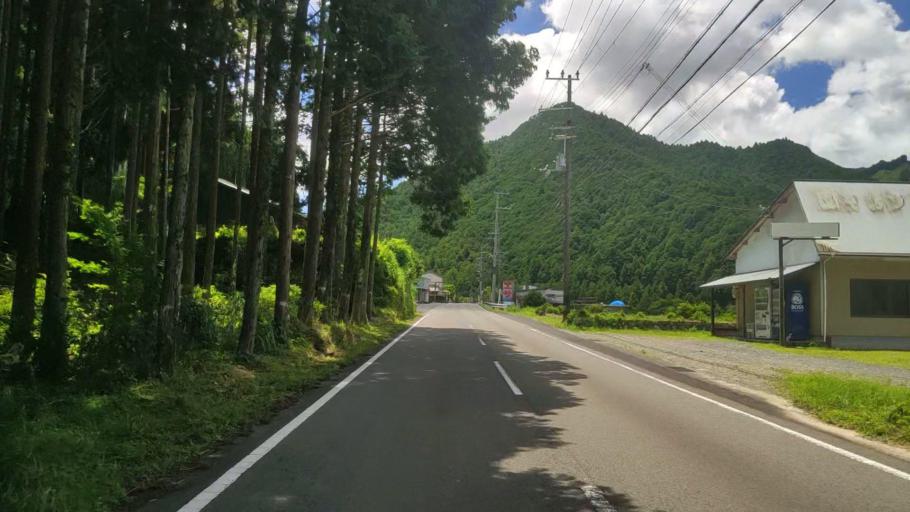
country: JP
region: Mie
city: Owase
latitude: 33.9660
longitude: 136.0610
